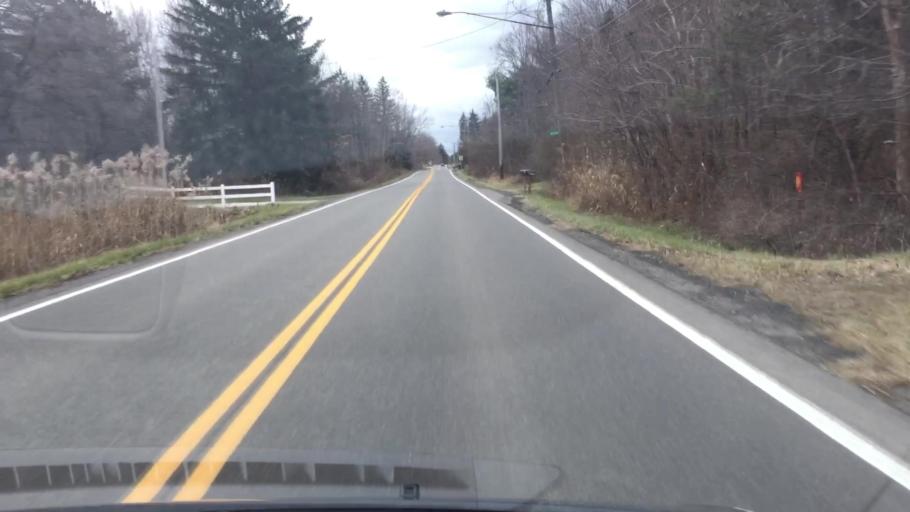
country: US
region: Ohio
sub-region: Summit County
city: Boston Heights
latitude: 41.2382
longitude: -81.4977
